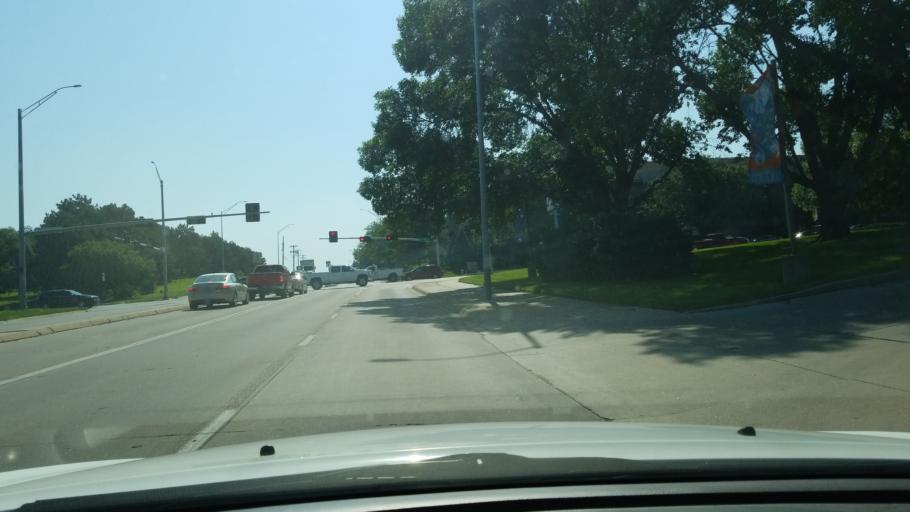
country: US
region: Nebraska
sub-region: Lancaster County
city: Lincoln
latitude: 40.7988
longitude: -96.6259
